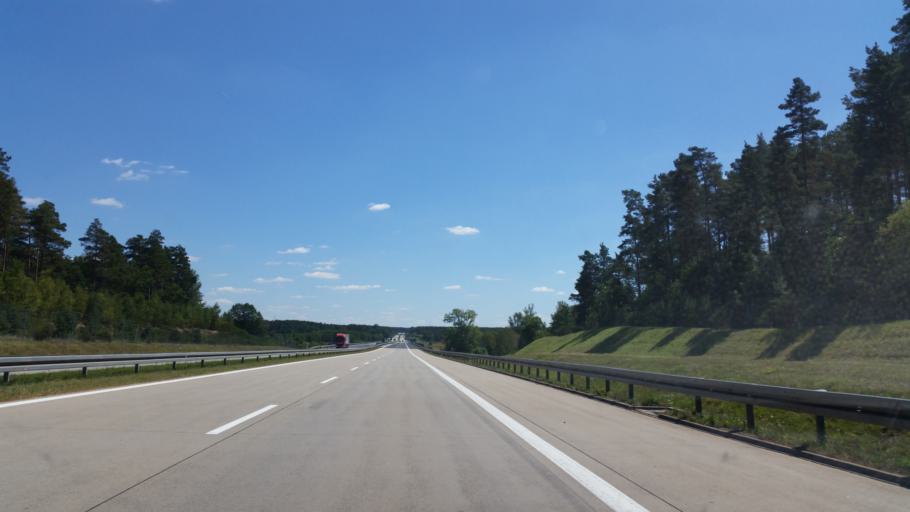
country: PL
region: Lower Silesian Voivodeship
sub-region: Powiat boleslawiecki
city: Boleslawiec
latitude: 51.3652
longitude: 15.5759
